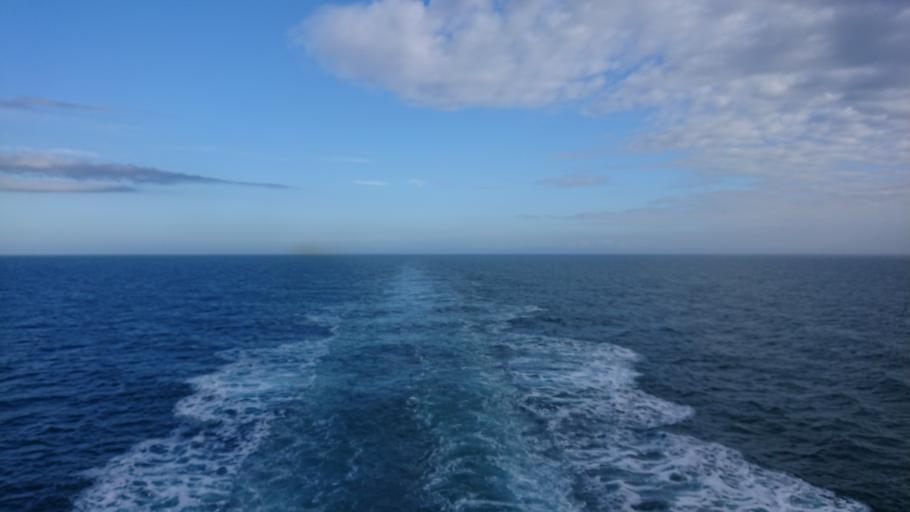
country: GB
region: Wales
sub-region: Pembrokeshire
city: Saint David's
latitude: 52.1342
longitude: -5.6141
